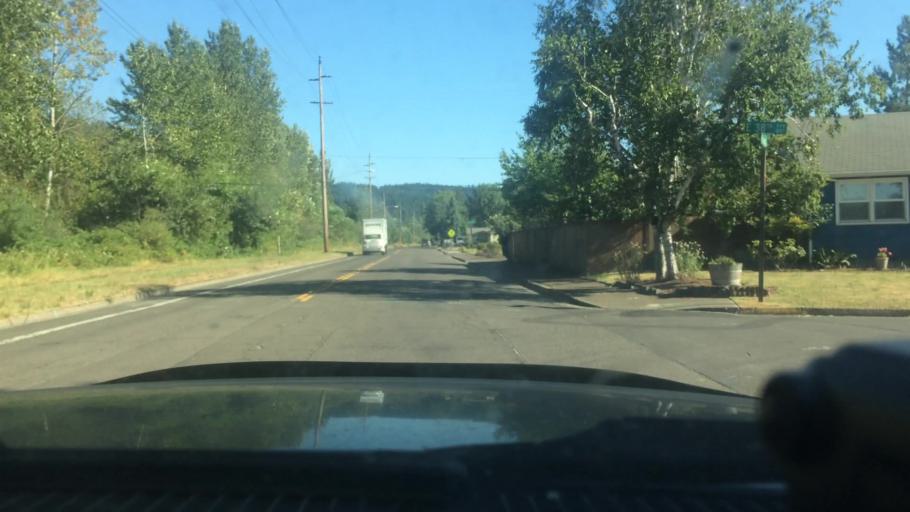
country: US
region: Oregon
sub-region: Lane County
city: Eugene
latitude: 44.0150
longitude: -123.0786
